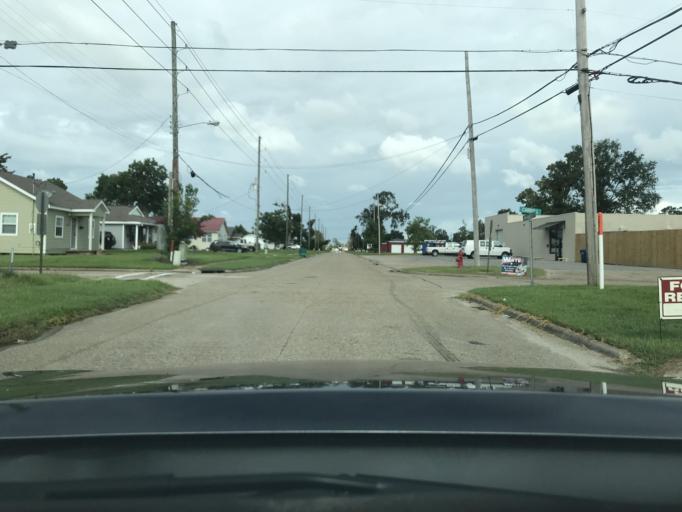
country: US
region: Louisiana
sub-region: Calcasieu Parish
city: Westlake
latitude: 30.2477
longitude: -93.2657
